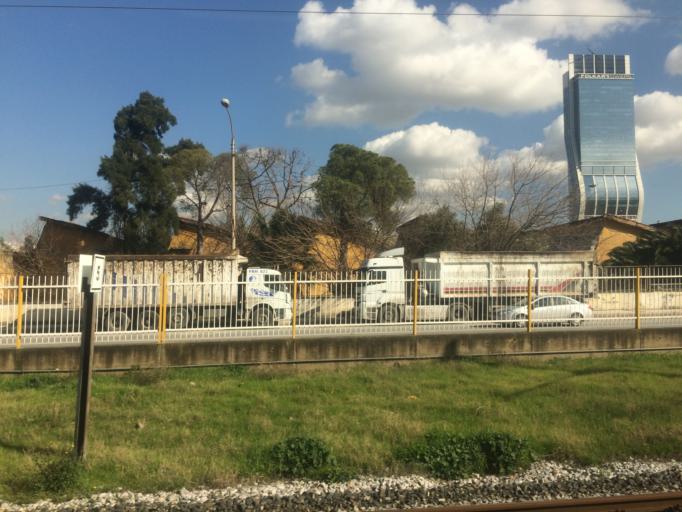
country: TR
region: Izmir
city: Izmir
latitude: 38.4549
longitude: 27.1702
